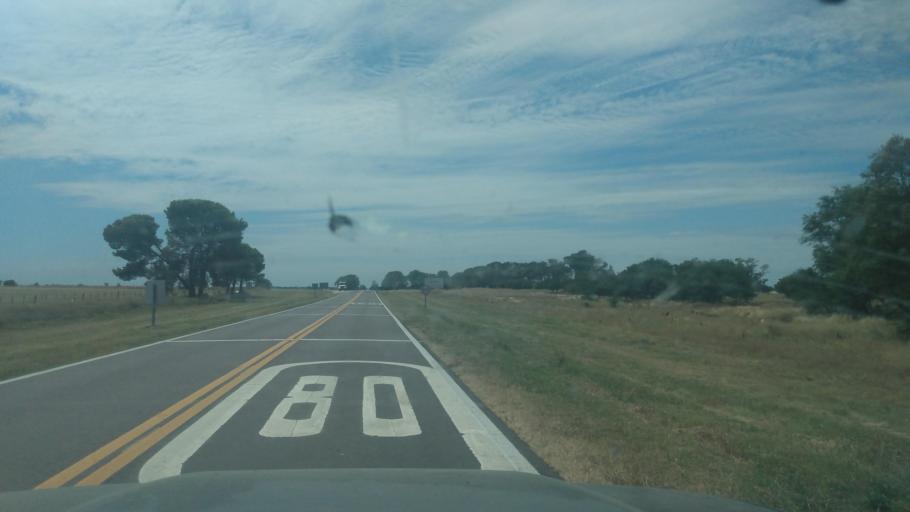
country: AR
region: La Pampa
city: Doblas
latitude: -37.1234
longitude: -64.2859
